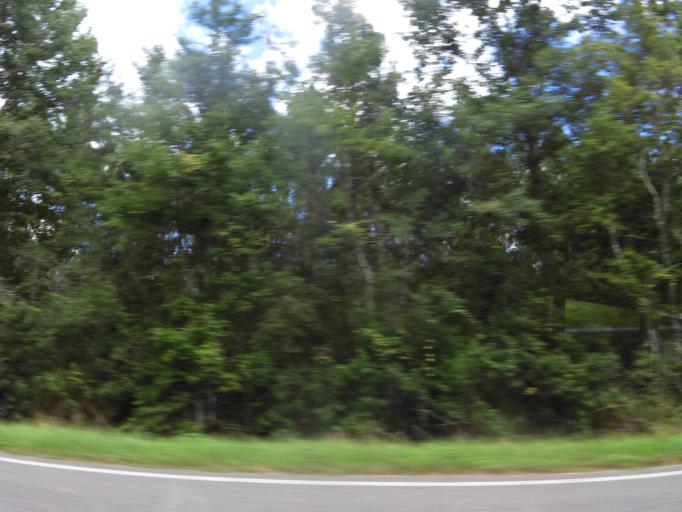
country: US
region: Florida
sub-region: Saint Johns County
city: Saint Augustine South
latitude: 29.8177
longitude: -81.4849
